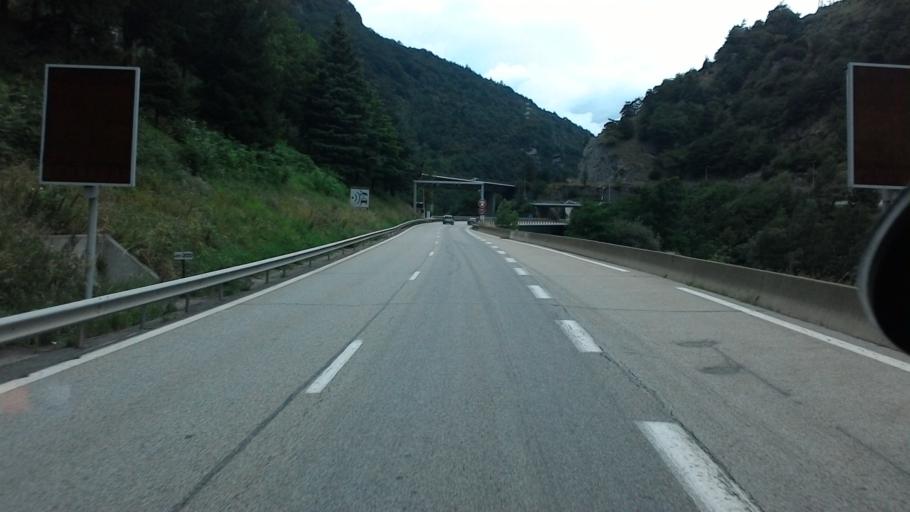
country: FR
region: Rhone-Alpes
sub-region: Departement de la Savoie
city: Moutiers
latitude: 45.4861
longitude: 6.5225
